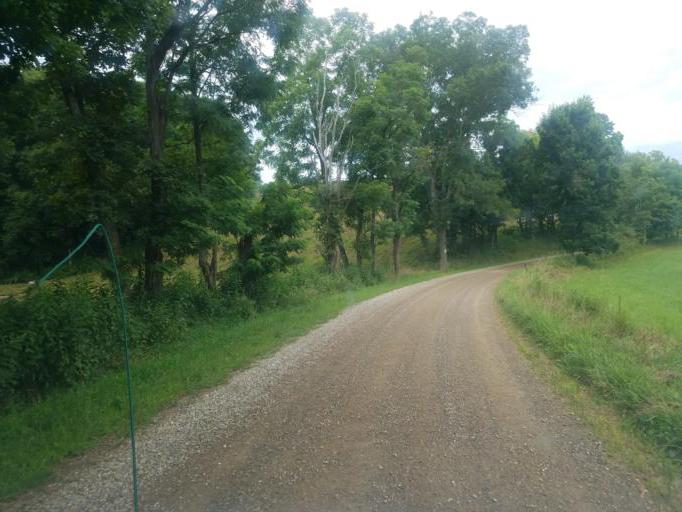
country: US
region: Ohio
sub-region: Knox County
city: Oak Hill
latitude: 40.3140
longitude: -82.1034
